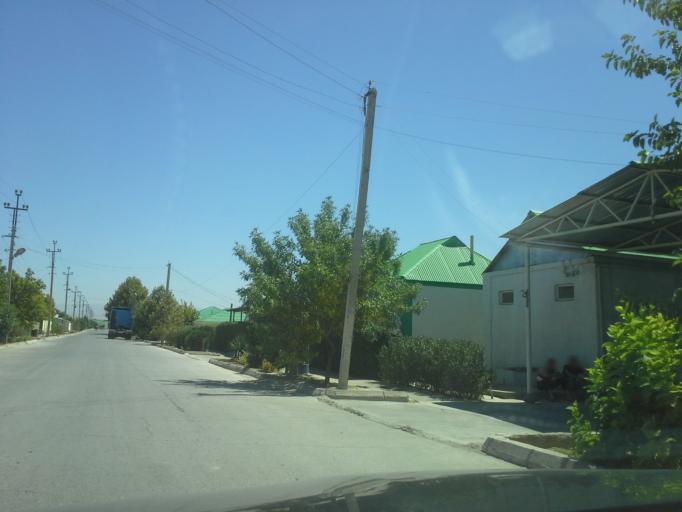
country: TM
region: Ahal
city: Abadan
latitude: 38.0435
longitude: 58.2163
